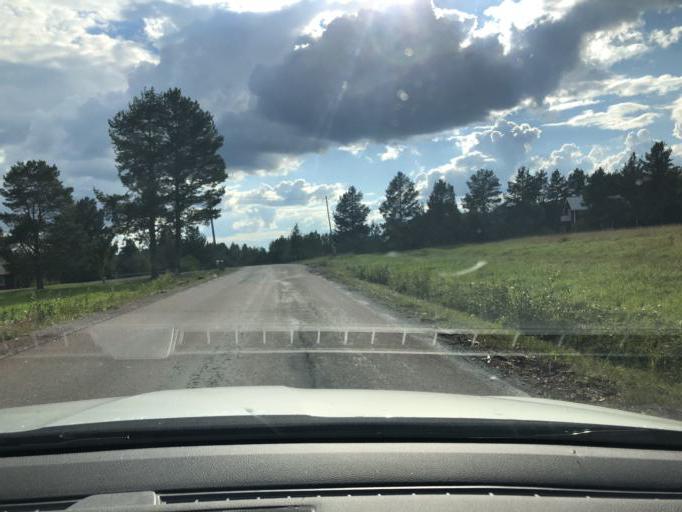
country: SE
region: Vaesternorrland
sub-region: Solleftea Kommun
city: Solleftea
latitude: 63.1967
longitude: 17.0871
